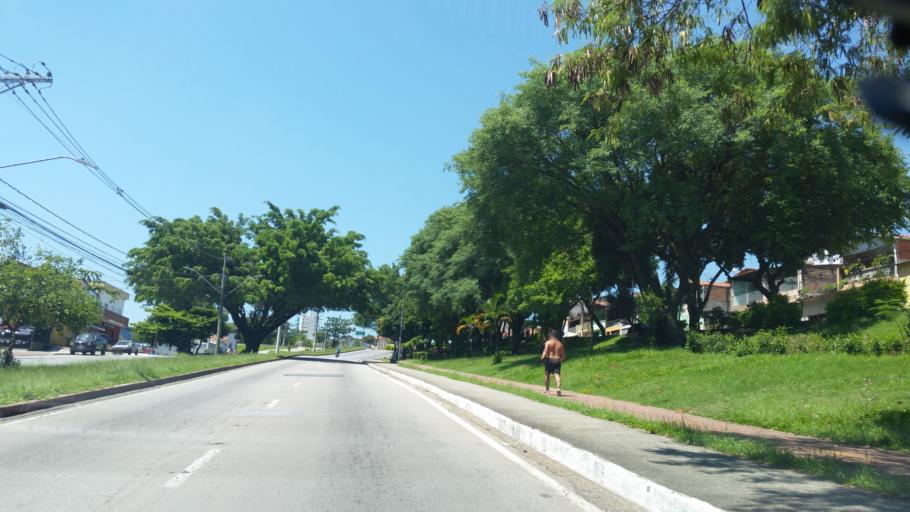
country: BR
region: Sao Paulo
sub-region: Sao Jose Dos Campos
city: Sao Jose dos Campos
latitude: -23.1710
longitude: -45.8118
